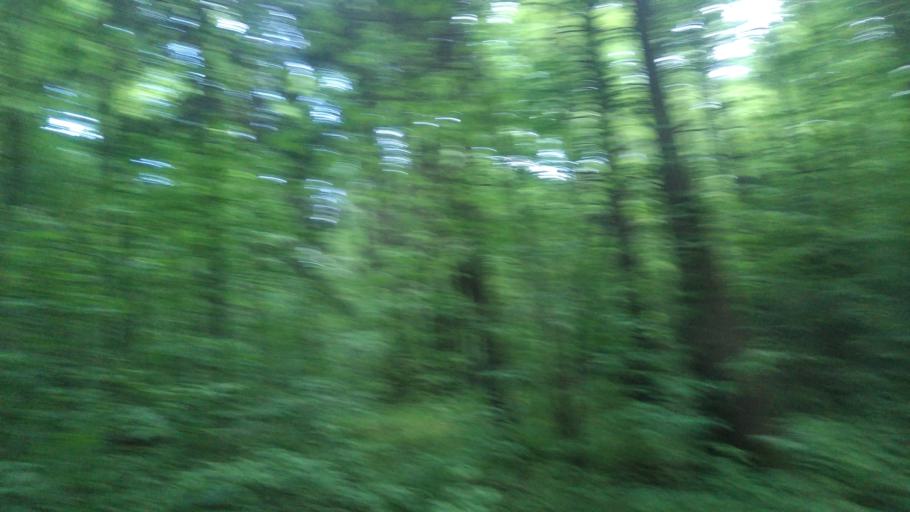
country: RU
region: Perm
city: Ferma
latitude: 57.9680
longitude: 56.3438
